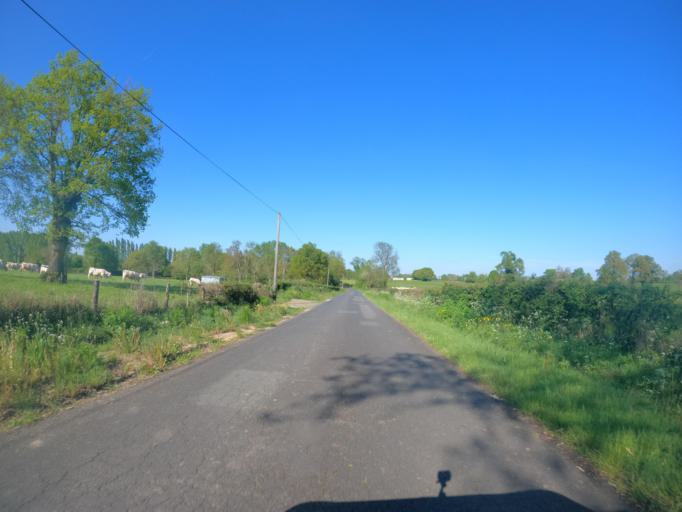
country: FR
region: Poitou-Charentes
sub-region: Departement des Deux-Sevres
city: La Chapelle-Saint-Laurent
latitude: 46.6847
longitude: -0.5145
